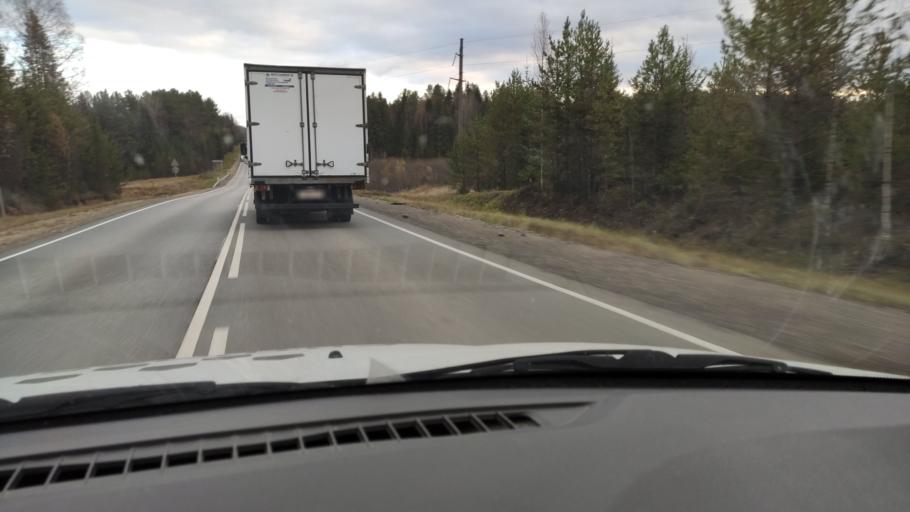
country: RU
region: Kirov
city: Chernaya Kholunitsa
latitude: 58.8487
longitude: 51.7426
